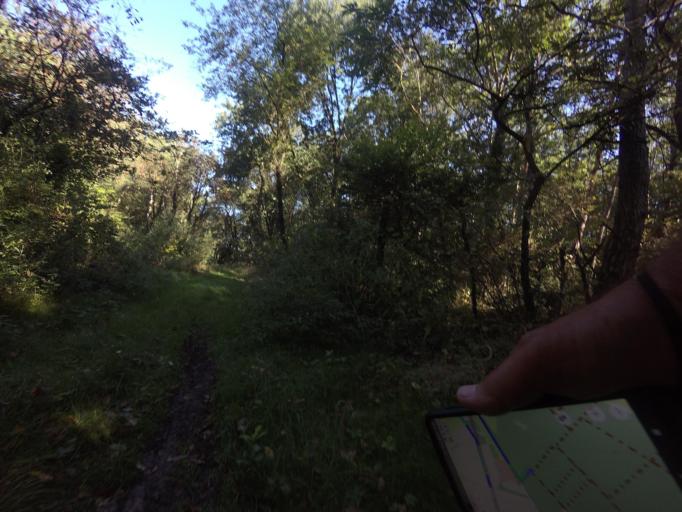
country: DE
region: Lower Saxony
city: Wielen
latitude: 52.5461
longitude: 6.7076
